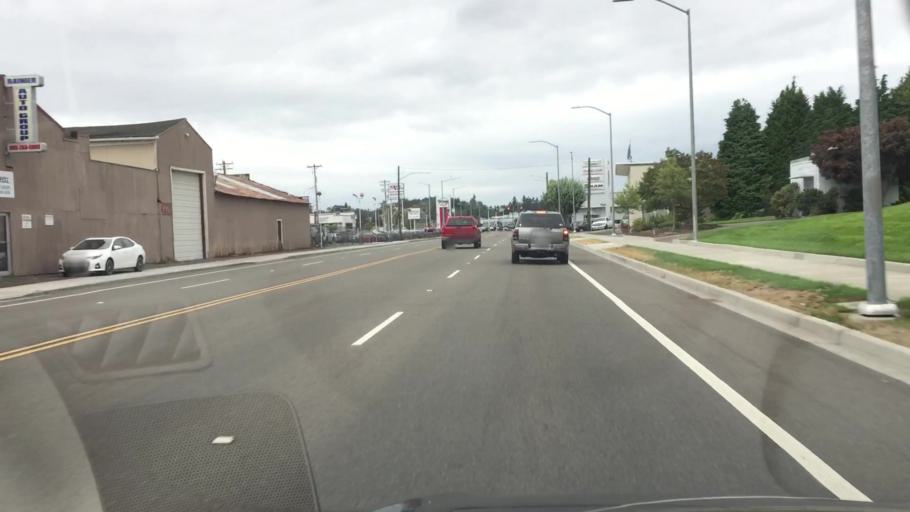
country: US
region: Washington
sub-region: Pierce County
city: Fircrest
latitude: 47.2177
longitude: -122.4842
